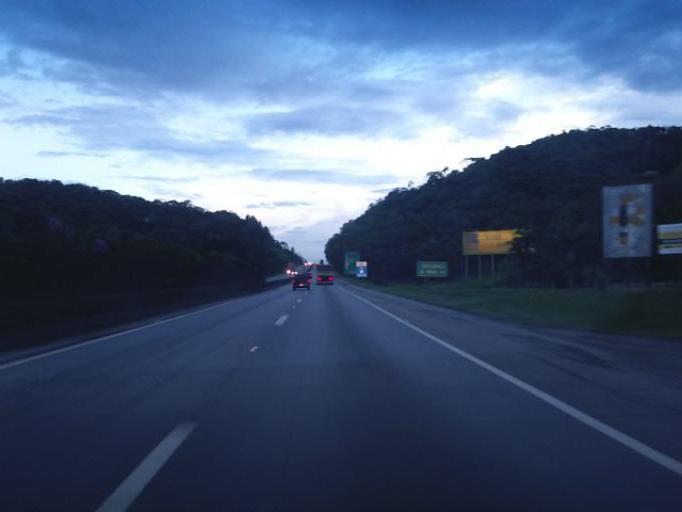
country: BR
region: Santa Catarina
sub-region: Joinville
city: Joinville
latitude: -26.2206
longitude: -48.9163
